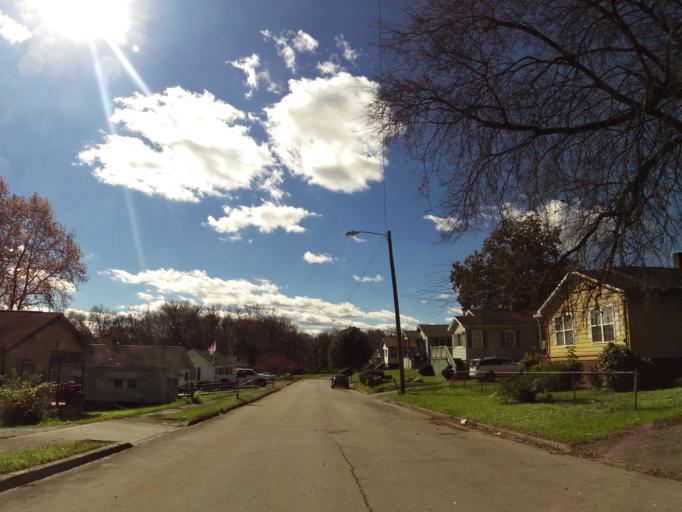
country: US
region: Tennessee
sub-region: Blount County
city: Alcoa
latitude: 35.7731
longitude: -83.9803
